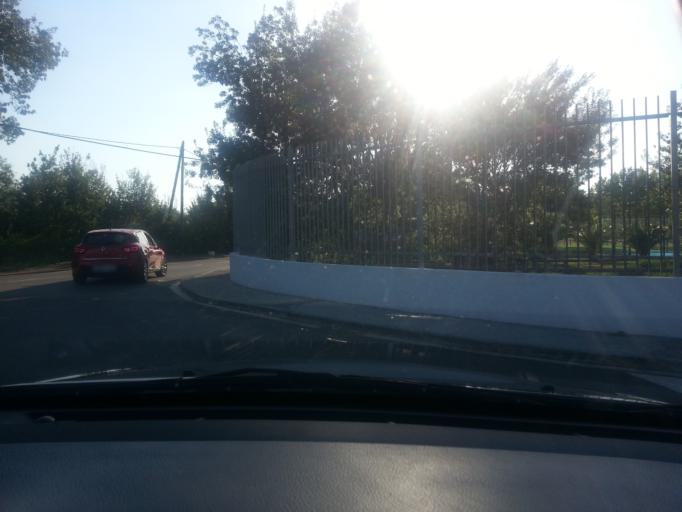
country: ES
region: Catalonia
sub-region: Provincia de Girona
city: Pals
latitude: 42.0099
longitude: 3.1885
